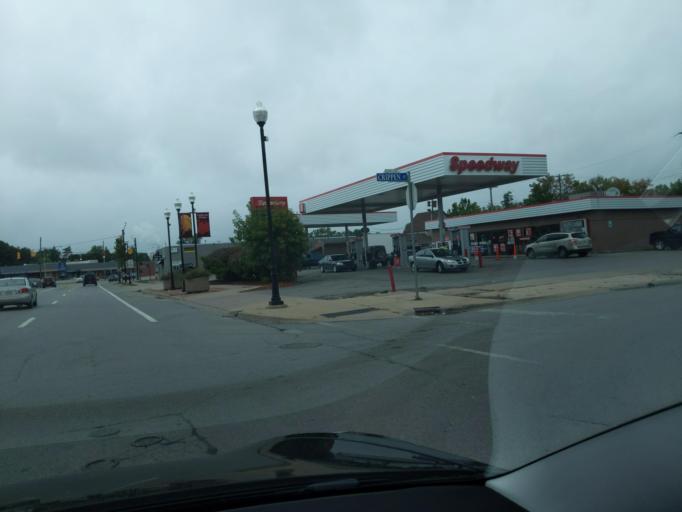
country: US
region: Michigan
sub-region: Wexford County
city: Cadillac
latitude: 44.2556
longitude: -85.4037
